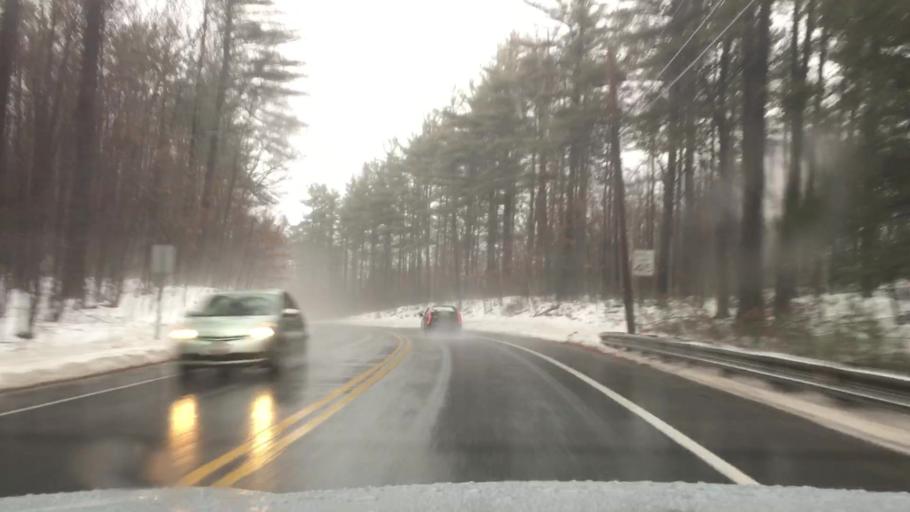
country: US
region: Massachusetts
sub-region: Franklin County
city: Wendell
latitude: 42.5070
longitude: -72.3287
